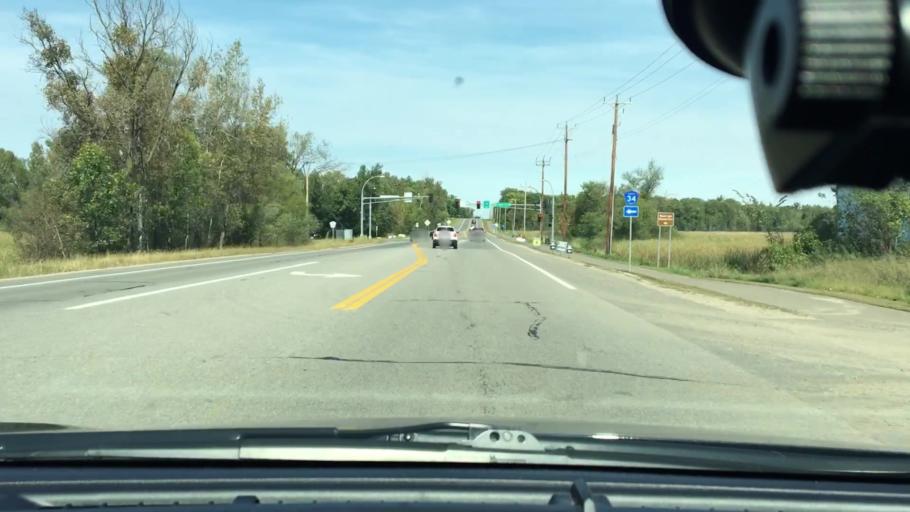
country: US
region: Minnesota
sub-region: Wright County
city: Hanover
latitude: 45.1605
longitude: -93.6660
